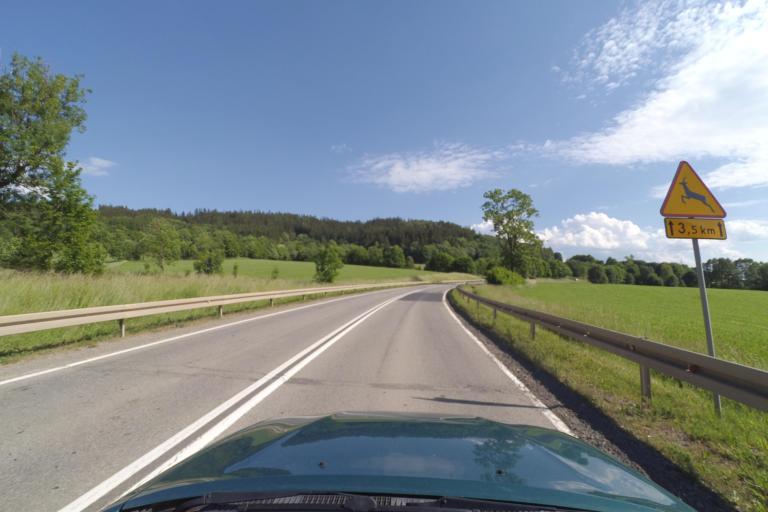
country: PL
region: Lower Silesian Voivodeship
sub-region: Powiat kamiennogorski
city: Lubawka
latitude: 50.7436
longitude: 16.0131
